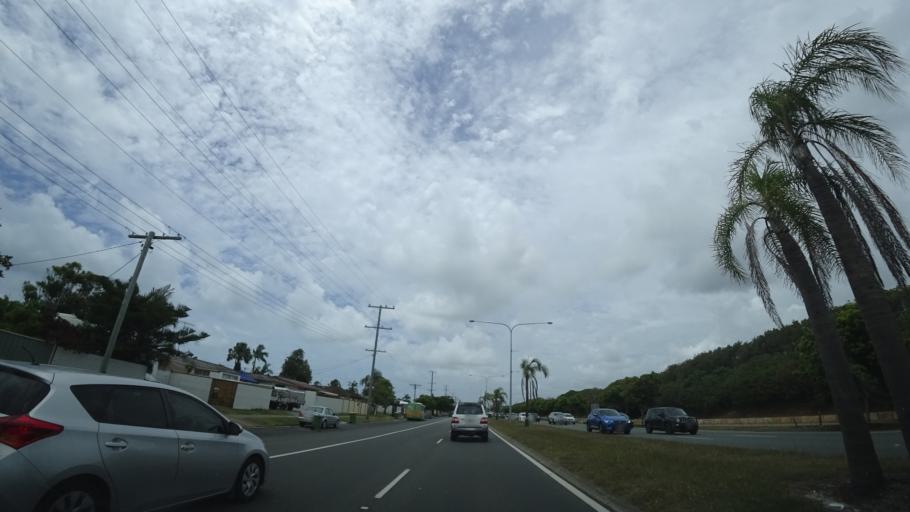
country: AU
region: Queensland
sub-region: Sunshine Coast
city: Mooloolaba
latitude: -26.7161
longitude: 153.1299
